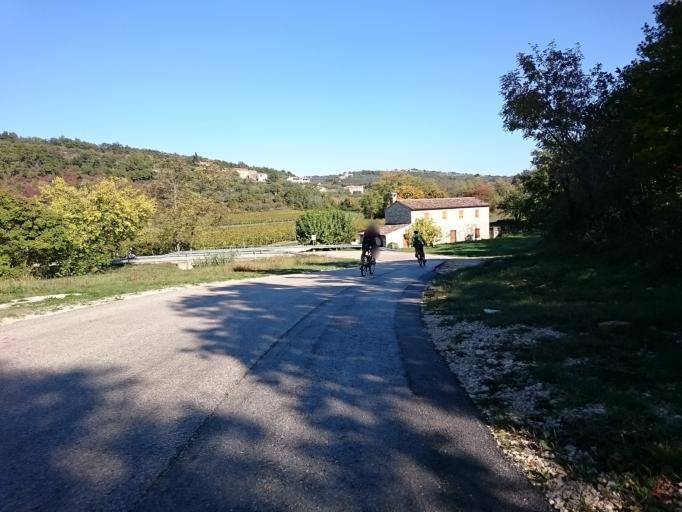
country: HR
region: Istarska
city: Buje
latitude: 45.4344
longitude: 13.6916
